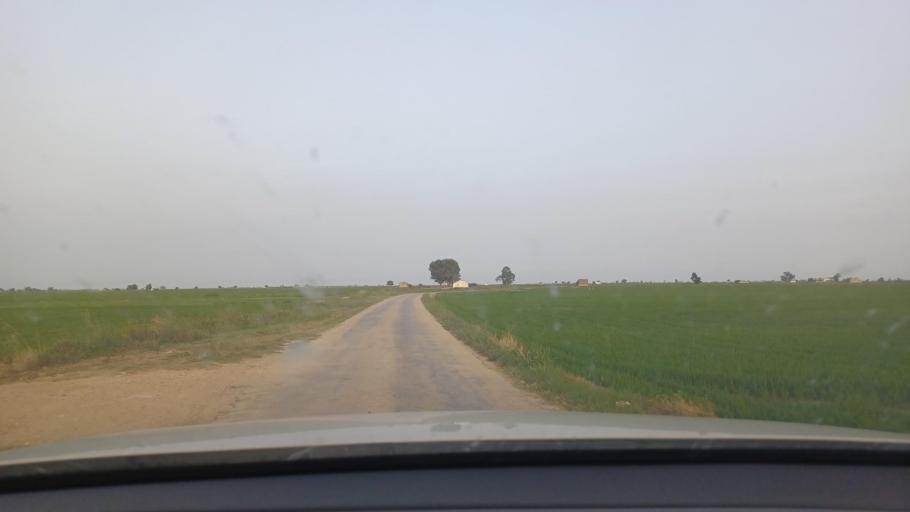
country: ES
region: Catalonia
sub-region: Provincia de Tarragona
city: Amposta
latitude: 40.6988
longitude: 0.6449
